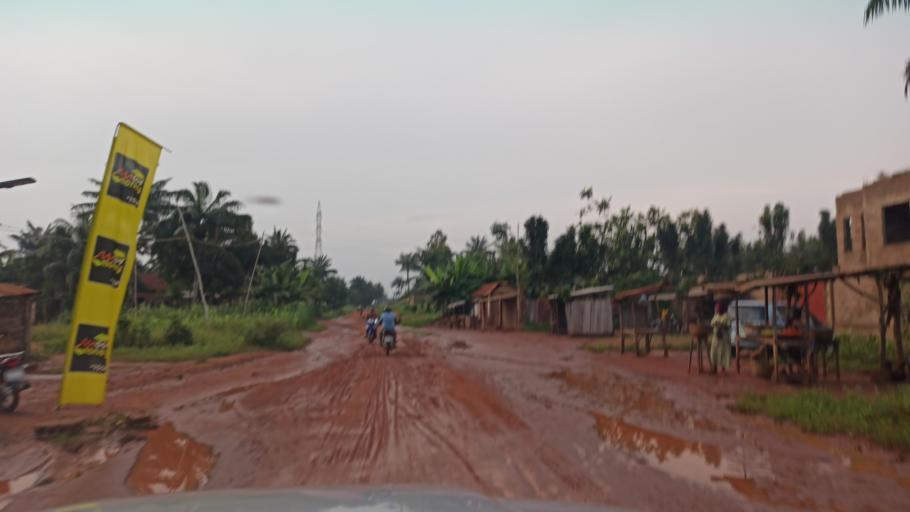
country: BJ
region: Queme
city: Porto-Novo
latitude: 6.5412
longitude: 2.6224
